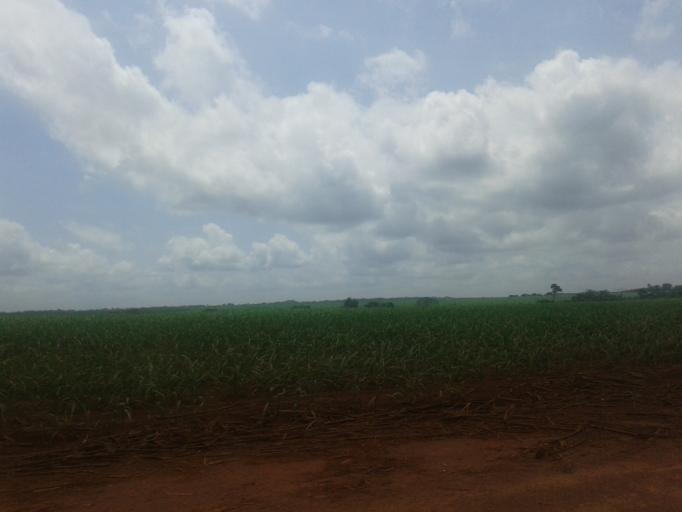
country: CM
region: Centre
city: Mbandjok
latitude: 4.4459
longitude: 11.9444
